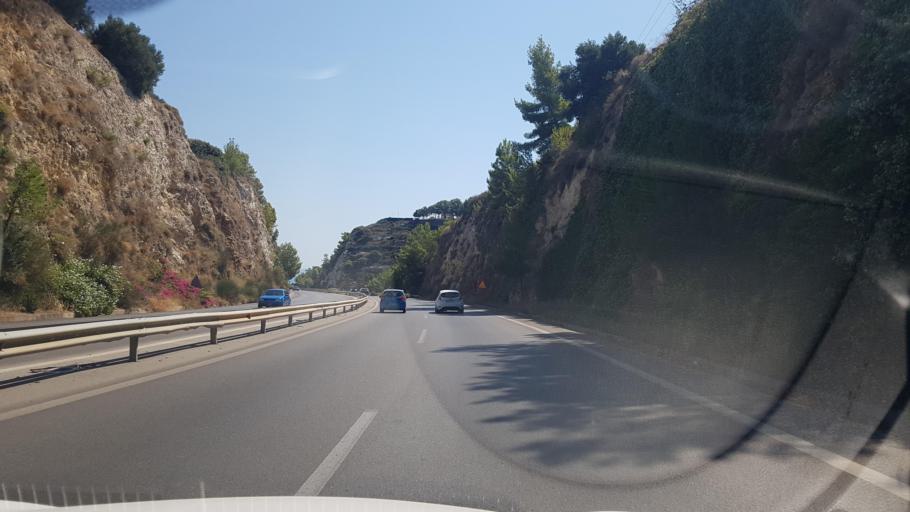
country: GR
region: Crete
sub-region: Nomos Rethymnis
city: Rethymno
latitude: 35.3555
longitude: 24.4798
